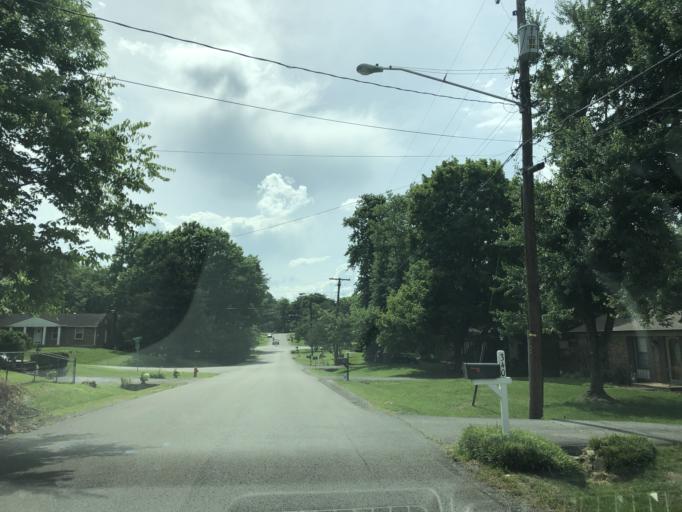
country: US
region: Tennessee
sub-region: Davidson County
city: Oak Hill
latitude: 36.0801
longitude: -86.7430
